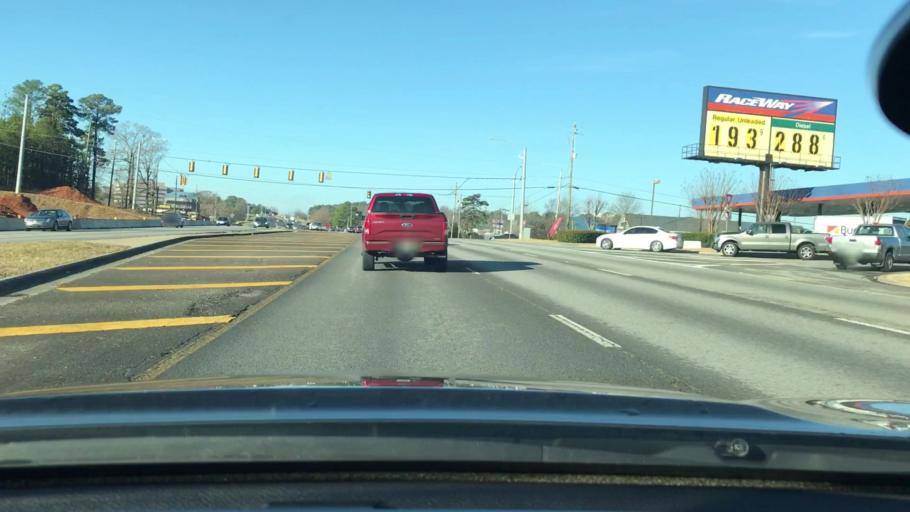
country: US
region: Alabama
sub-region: Shelby County
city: Lake Purdy
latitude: 33.4193
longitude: -86.6738
